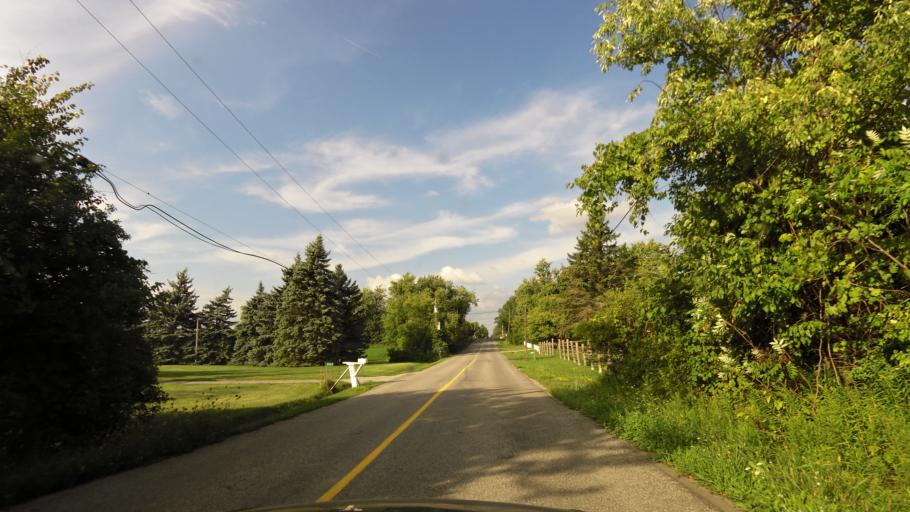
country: CA
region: Ontario
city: Burlington
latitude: 43.3788
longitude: -79.8722
